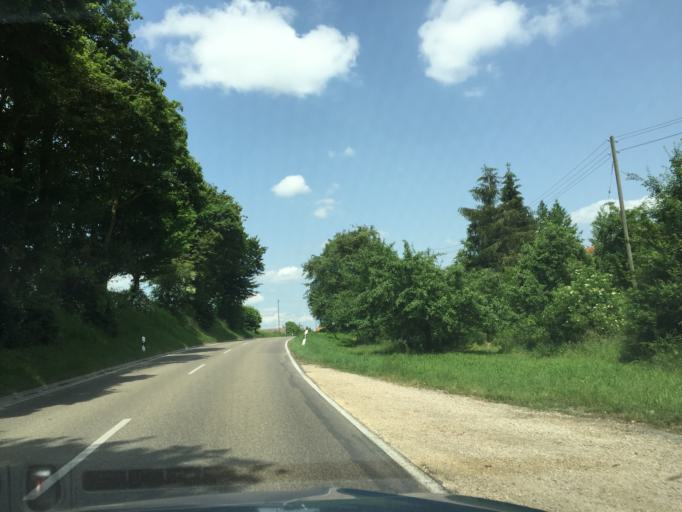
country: DE
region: Bavaria
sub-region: Swabia
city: Zusamaltheim
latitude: 48.5261
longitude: 10.6313
